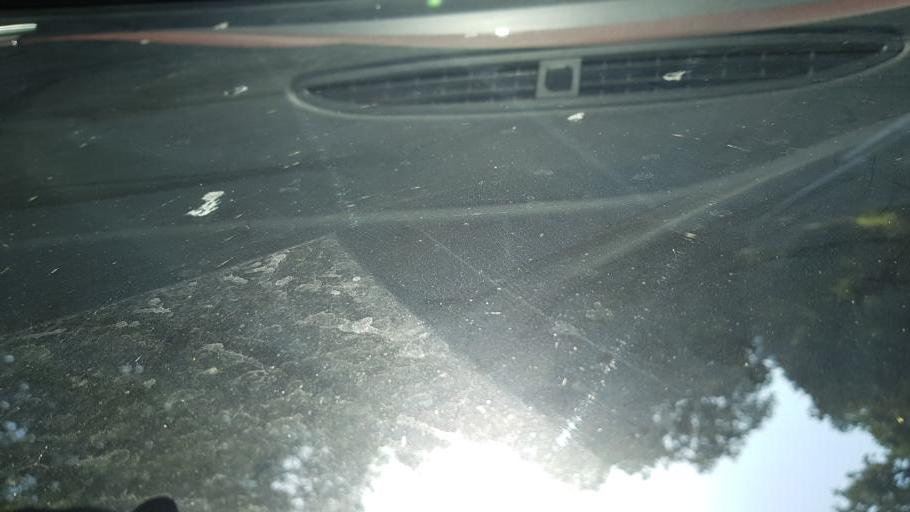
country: ES
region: Castille and Leon
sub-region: Provincia de Segovia
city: San Ildefonso
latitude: 40.8672
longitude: -4.0241
